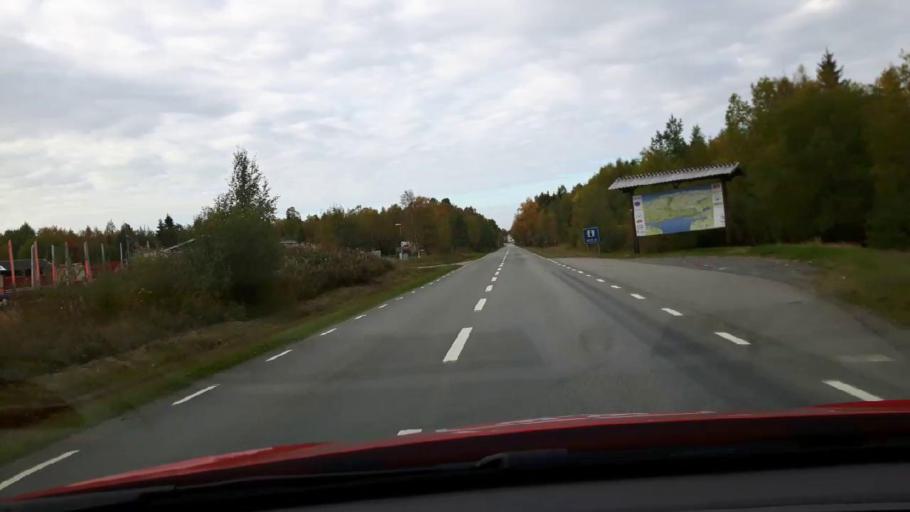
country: SE
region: Jaemtland
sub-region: Krokoms Kommun
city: Krokom
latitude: 63.1694
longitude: 14.1074
